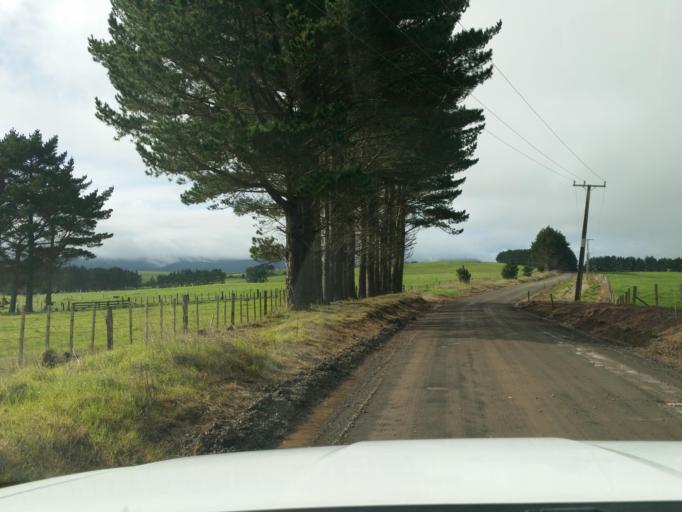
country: NZ
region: Northland
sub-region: Kaipara District
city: Dargaville
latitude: -35.7547
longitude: 173.6052
